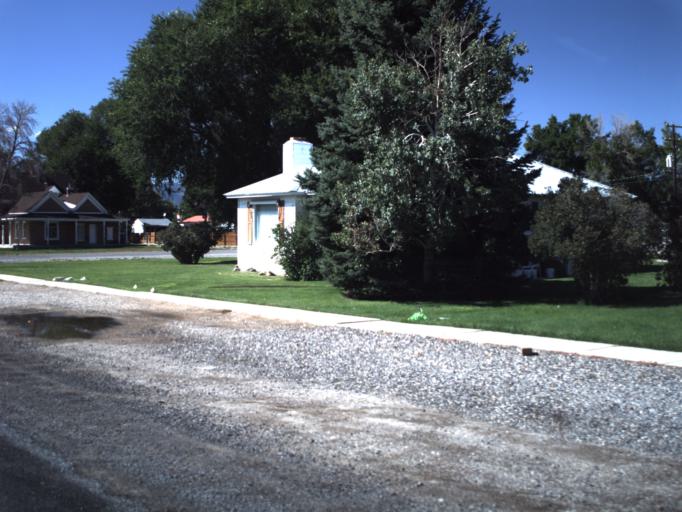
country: US
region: Utah
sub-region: Beaver County
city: Beaver
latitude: 38.2770
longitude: -112.6354
